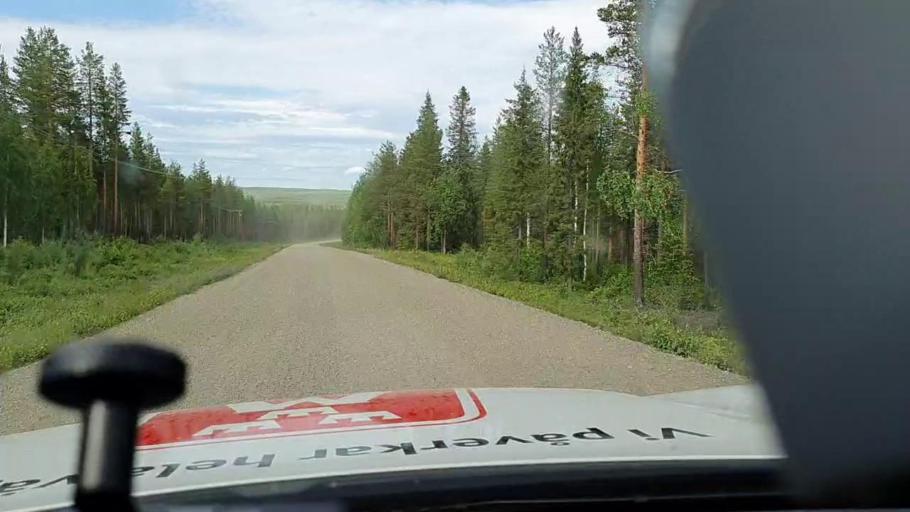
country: SE
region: Norrbotten
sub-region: Alvsbyns Kommun
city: AElvsbyn
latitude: 66.1428
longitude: 21.0179
